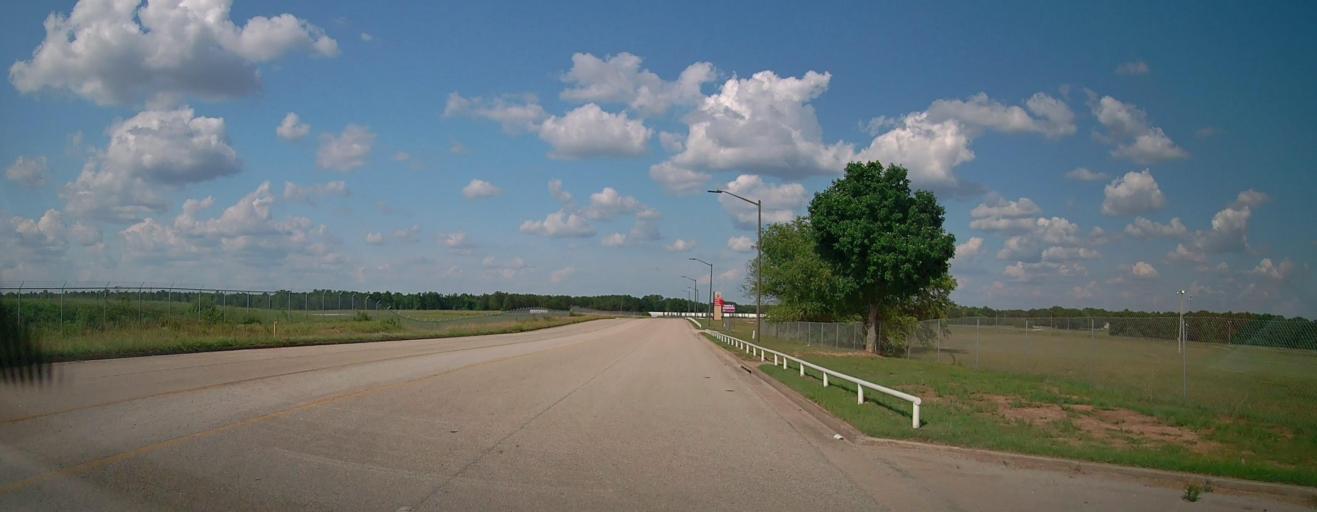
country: US
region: Georgia
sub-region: Henry County
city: Hampton
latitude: 33.3921
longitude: -84.3240
